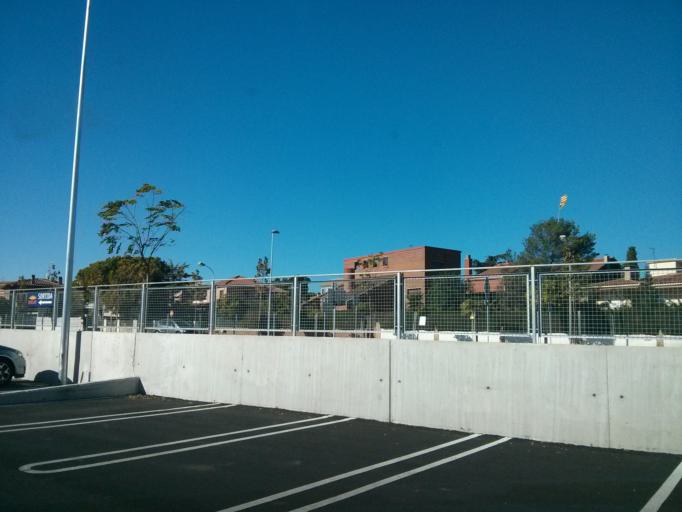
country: ES
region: Catalonia
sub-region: Provincia de Tarragona
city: El Vendrell
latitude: 41.2145
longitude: 1.5291
